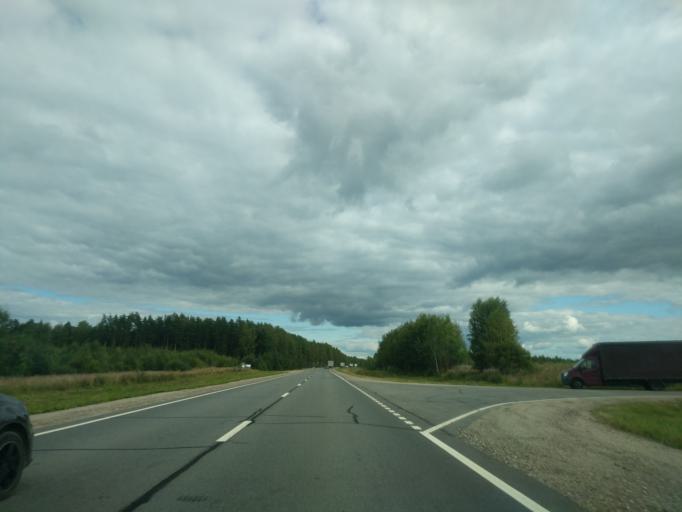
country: RU
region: Kostroma
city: Sudislavl'
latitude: 57.8166
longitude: 41.9592
